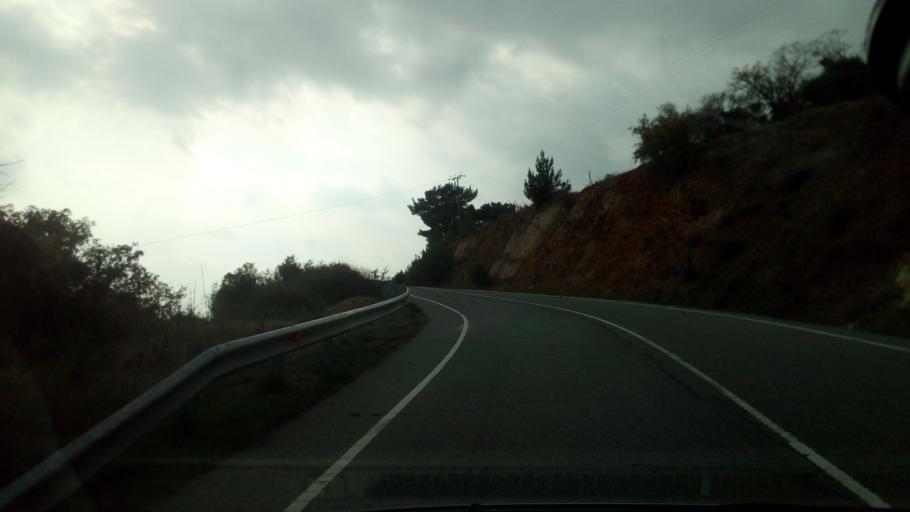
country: CY
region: Lefkosia
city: Lythrodontas
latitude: 34.8763
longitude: 33.2645
